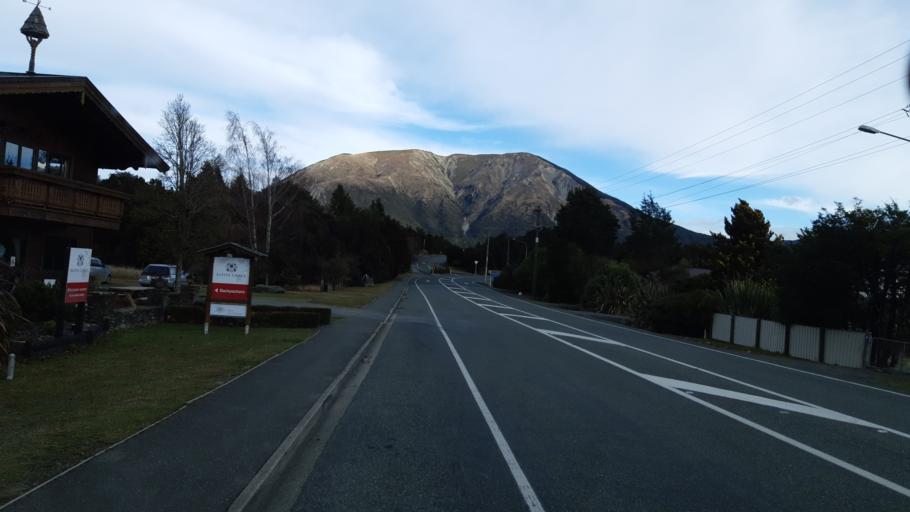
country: NZ
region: Tasman
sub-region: Tasman District
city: Wakefield
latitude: -41.8021
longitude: 172.8470
